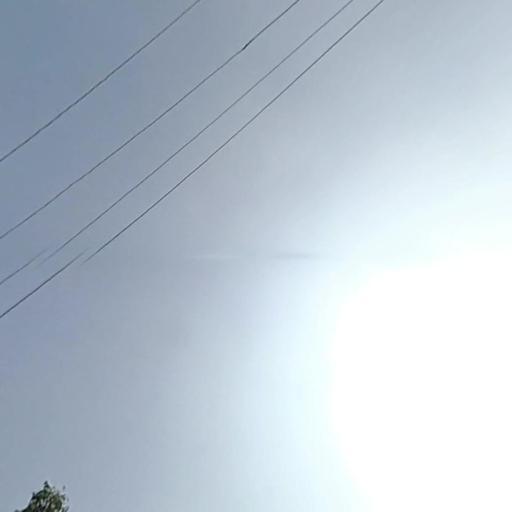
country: IN
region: Telangana
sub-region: Nalgonda
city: Nalgonda
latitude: 17.1858
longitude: 79.1262
